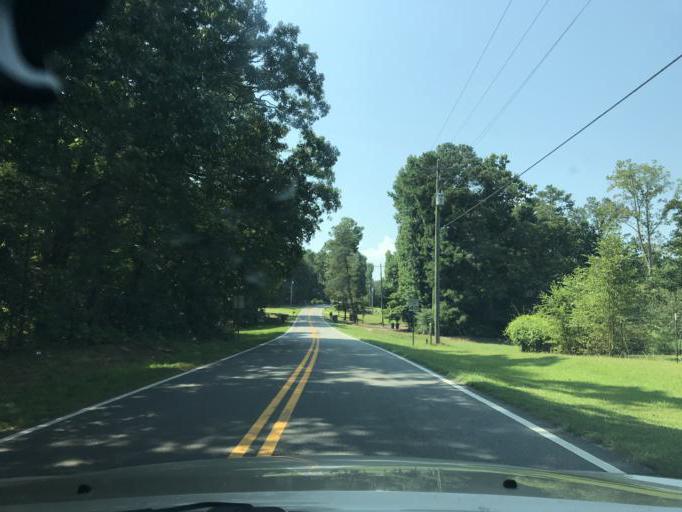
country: US
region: Georgia
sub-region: Hall County
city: Flowery Branch
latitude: 34.2364
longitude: -83.9977
